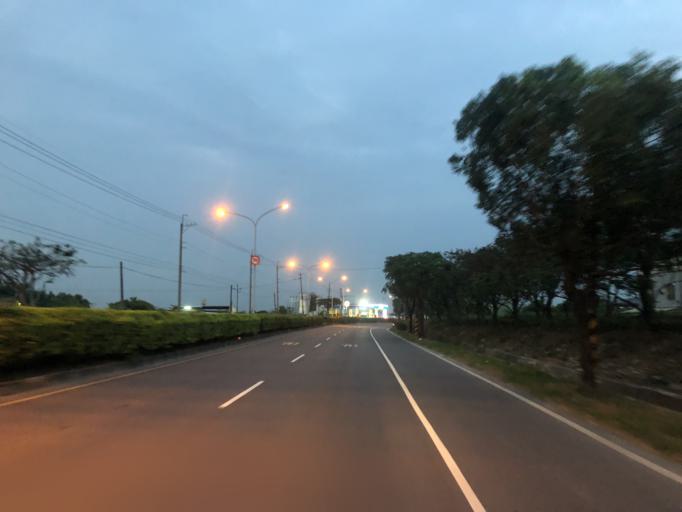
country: TW
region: Taiwan
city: Yujing
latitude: 23.1401
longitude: 120.3240
